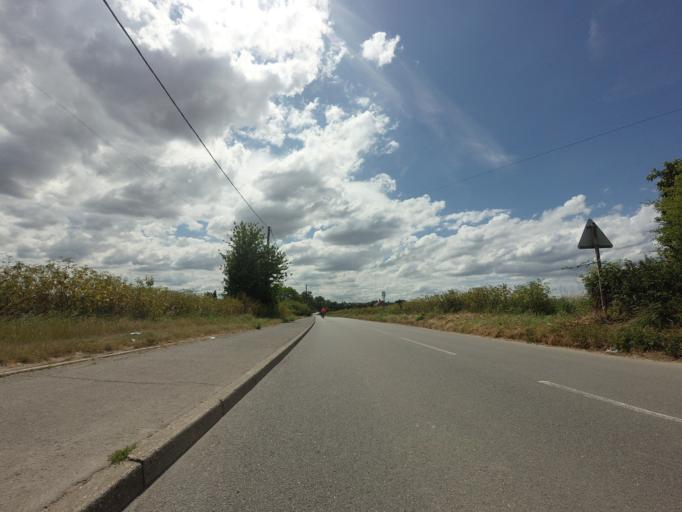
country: GB
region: England
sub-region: Kent
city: Hoo
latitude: 51.4267
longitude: 0.5761
